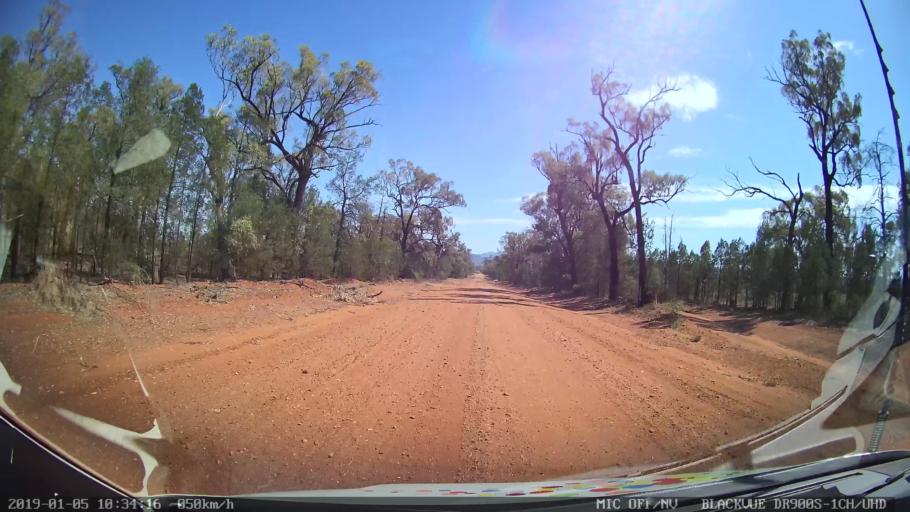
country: AU
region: New South Wales
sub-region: Gilgandra
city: Gilgandra
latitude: -31.4996
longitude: 148.9290
